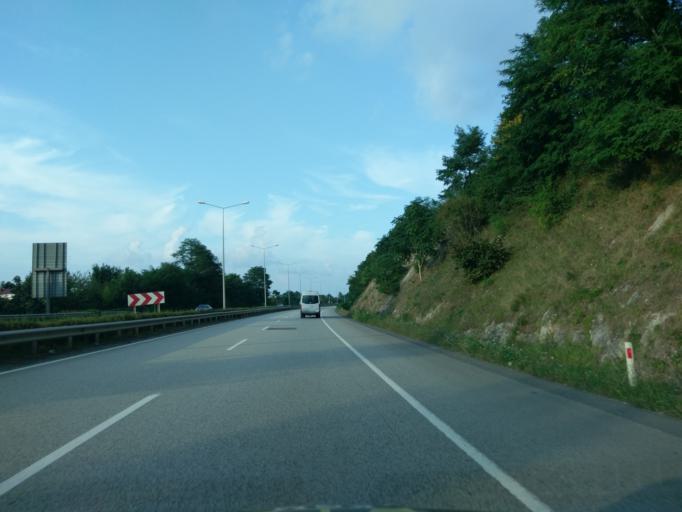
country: TR
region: Ordu
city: Ordu
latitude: 41.0111
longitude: 37.8314
